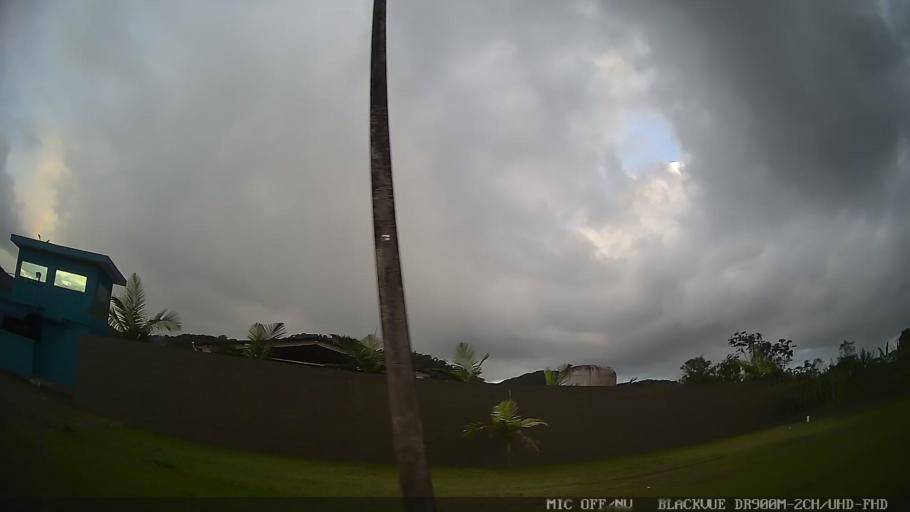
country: BR
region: Sao Paulo
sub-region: Itanhaem
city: Itanhaem
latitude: -24.0921
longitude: -46.7969
